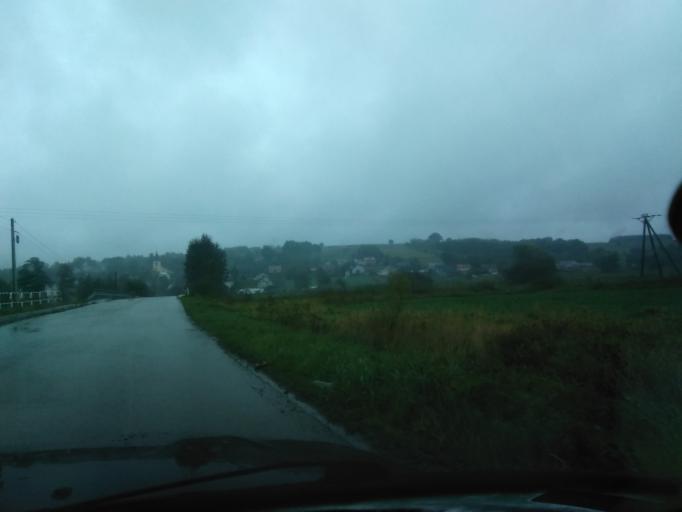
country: PL
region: Subcarpathian Voivodeship
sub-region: Powiat ropczycko-sedziszowski
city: Niedzwiada
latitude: 49.9960
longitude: 21.5566
